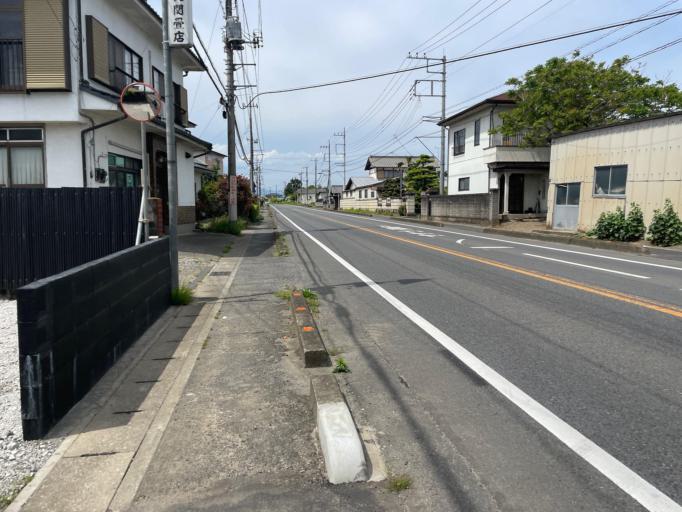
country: JP
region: Tochigi
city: Mibu
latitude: 36.4591
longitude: 139.7715
